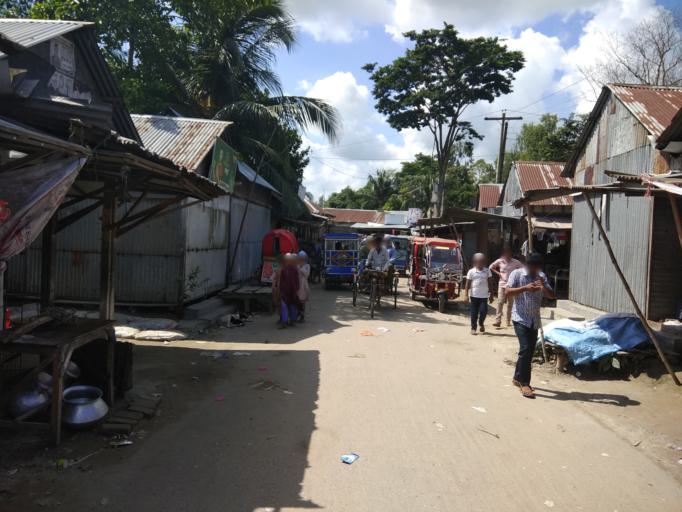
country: BD
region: Dhaka
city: Narayanganj
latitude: 23.4443
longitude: 90.4509
